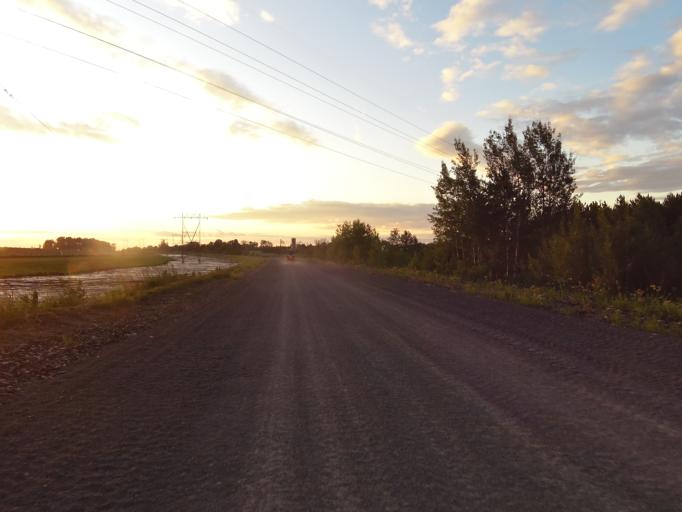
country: CA
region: Ontario
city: Arnprior
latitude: 45.4002
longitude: -76.3232
